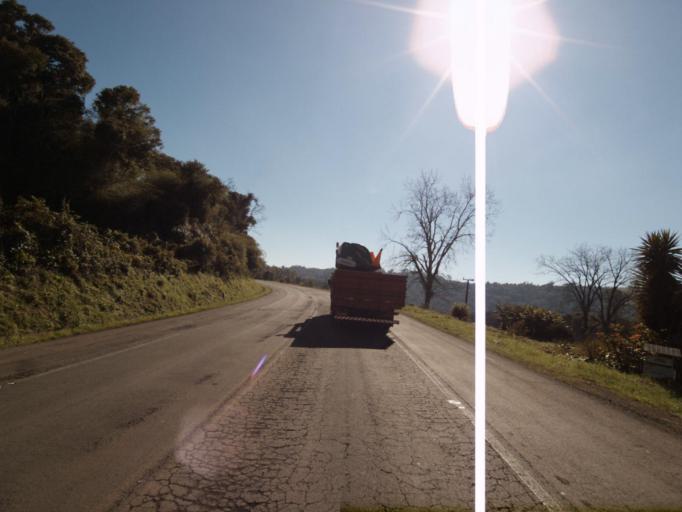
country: BR
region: Rio Grande do Sul
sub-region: Frederico Westphalen
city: Frederico Westphalen
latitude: -27.0636
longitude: -53.2209
